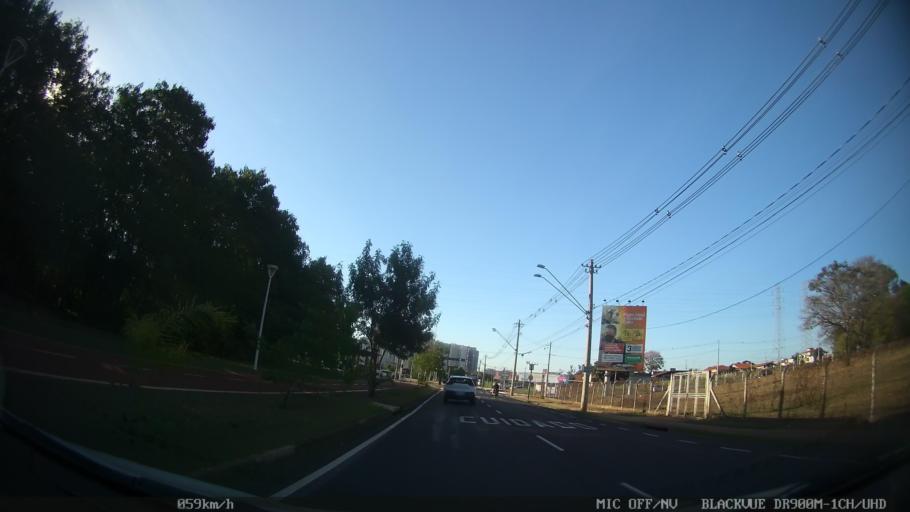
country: BR
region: Sao Paulo
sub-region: Sao Jose Do Rio Preto
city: Sao Jose do Rio Preto
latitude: -20.8434
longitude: -49.4111
